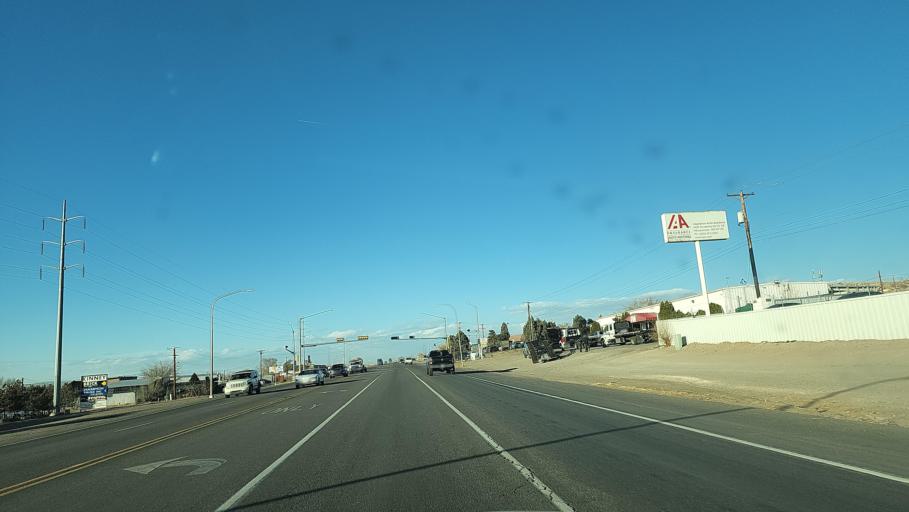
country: US
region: New Mexico
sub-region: Bernalillo County
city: South Valley
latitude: 35.0136
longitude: -106.6485
